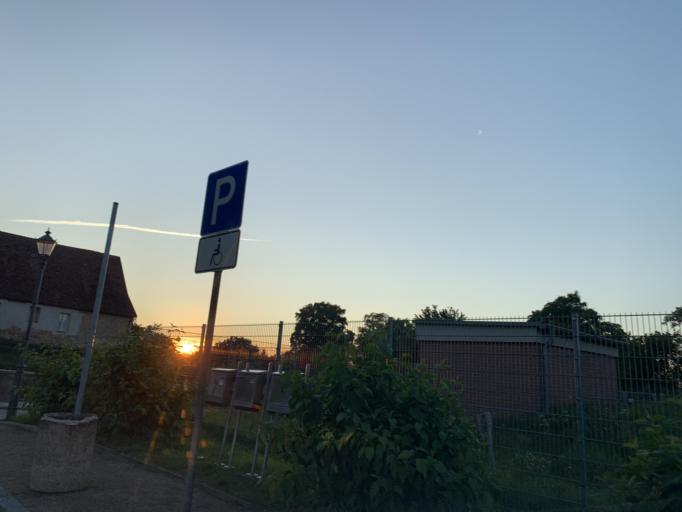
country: DE
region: Mecklenburg-Vorpommern
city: Burg Stargard
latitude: 53.4908
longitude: 13.3072
